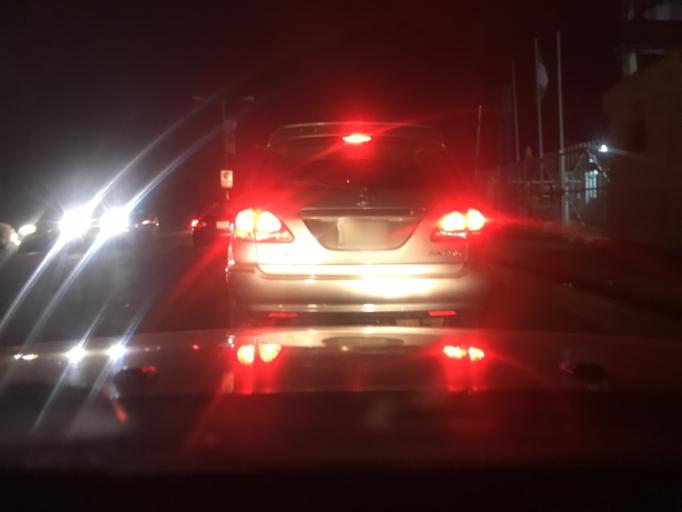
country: NG
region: Lagos
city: Agege
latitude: 6.5959
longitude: 3.2886
